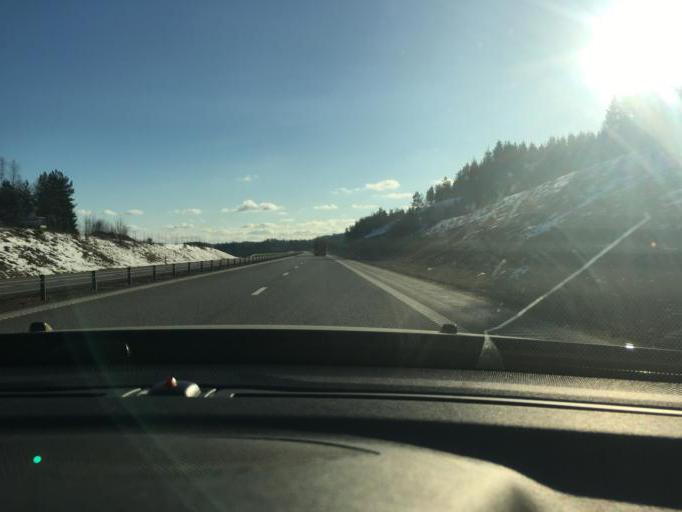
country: SE
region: Vaestra Goetaland
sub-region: Boras Kommun
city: Dalsjofors
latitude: 57.7710
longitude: 13.1137
